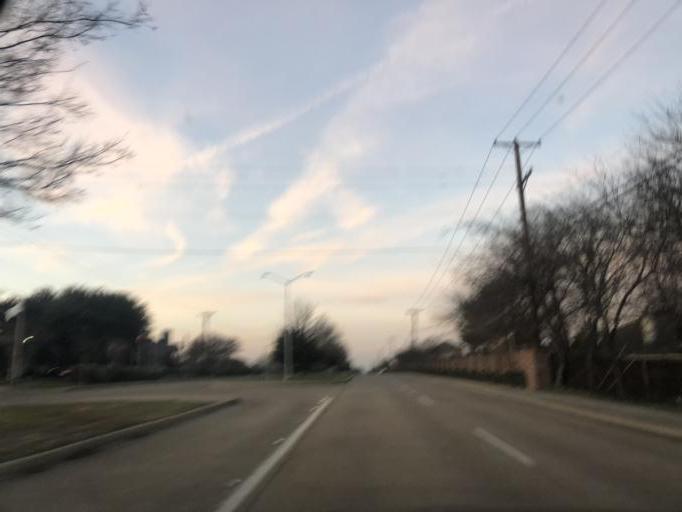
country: US
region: Texas
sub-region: Dallas County
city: Cedar Hill
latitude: 32.5921
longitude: -96.9264
